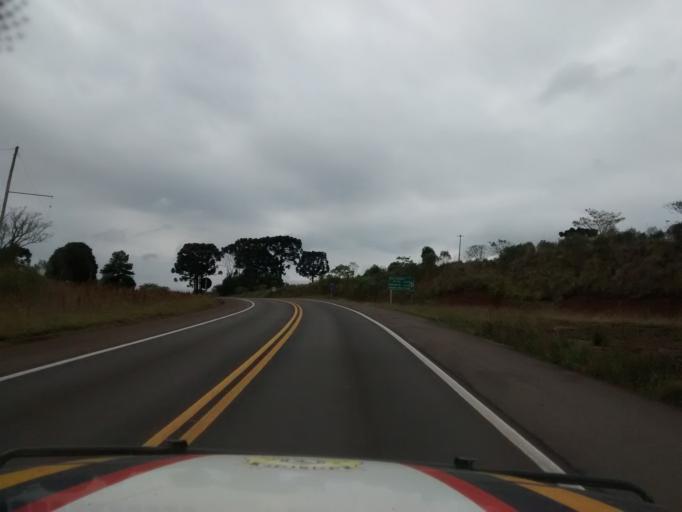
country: BR
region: Rio Grande do Sul
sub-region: Lagoa Vermelha
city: Lagoa Vermelha
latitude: -28.2266
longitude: -51.6154
